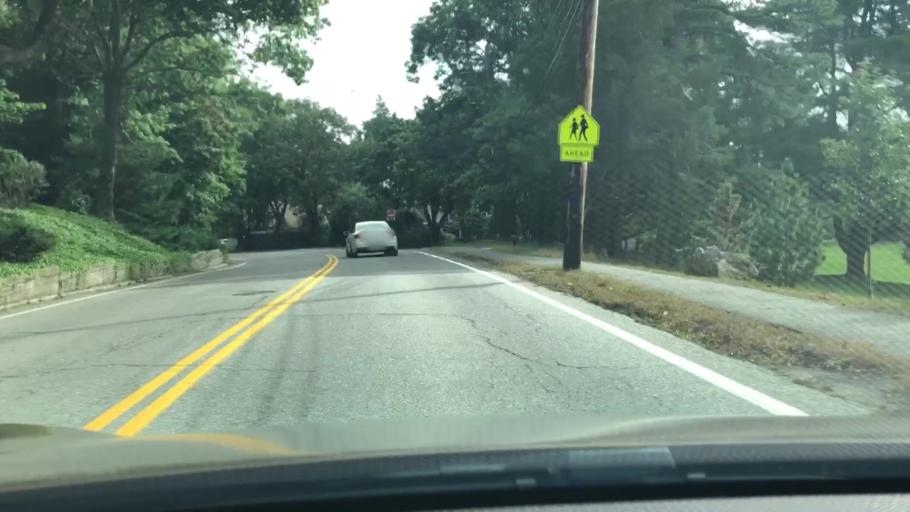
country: US
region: Massachusetts
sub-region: Middlesex County
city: Winchester
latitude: 42.4436
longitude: -71.1644
